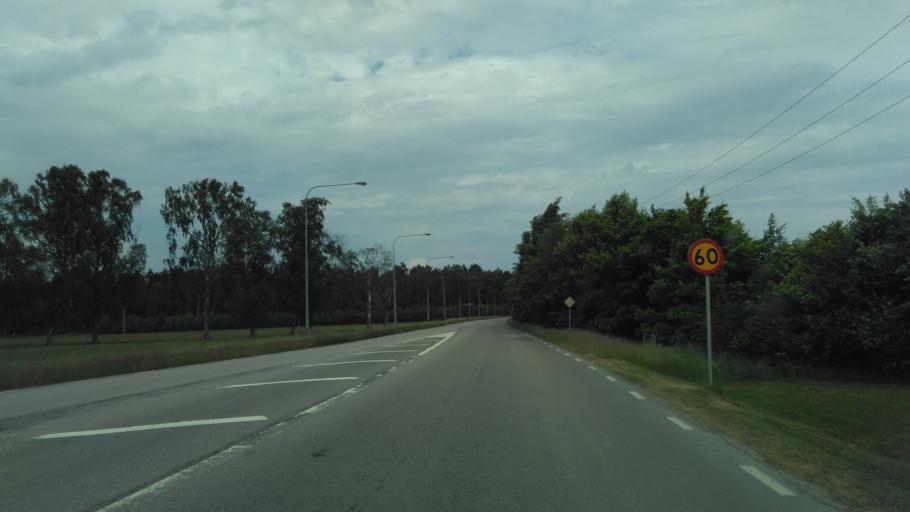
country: SE
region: Vaestra Goetaland
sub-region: Lidkopings Kommun
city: Lidkoping
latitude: 58.4814
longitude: 13.1371
